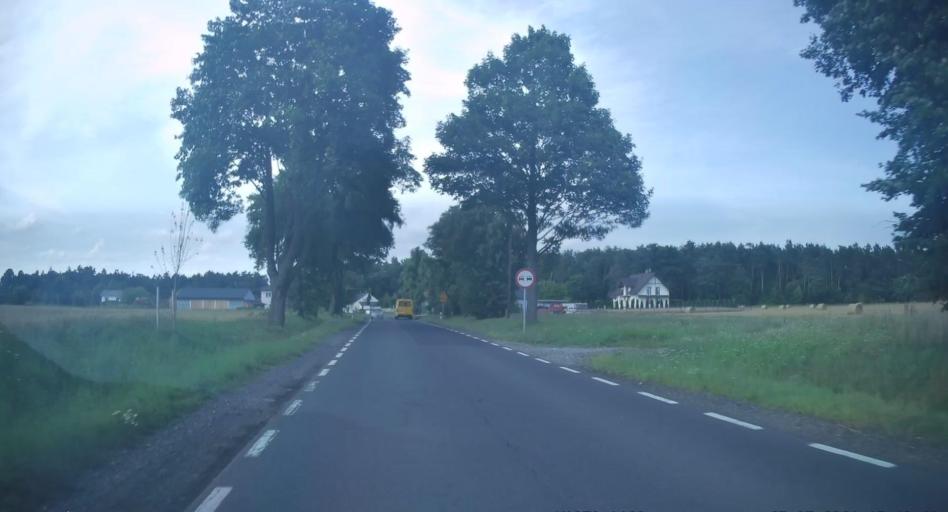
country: PL
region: Lodz Voivodeship
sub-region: Powiat rawski
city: Cieladz
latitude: 51.6809
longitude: 20.2676
